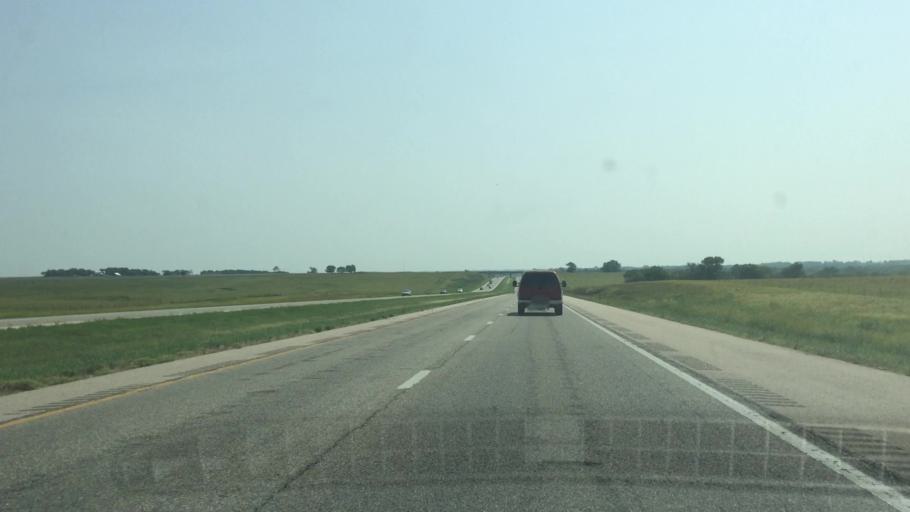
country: US
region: Kansas
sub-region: Osage County
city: Osage City
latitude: 38.4259
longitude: -95.7985
